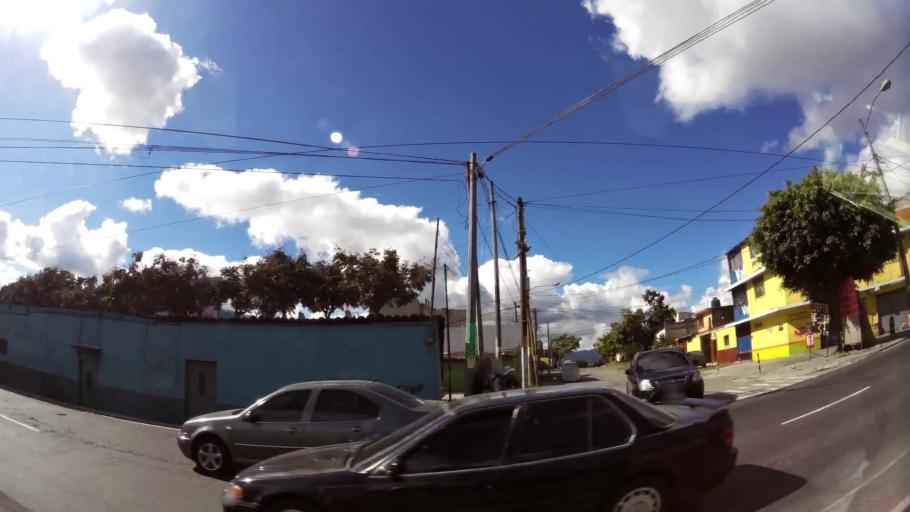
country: GT
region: Guatemala
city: Guatemala City
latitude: 14.5953
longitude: -90.5443
